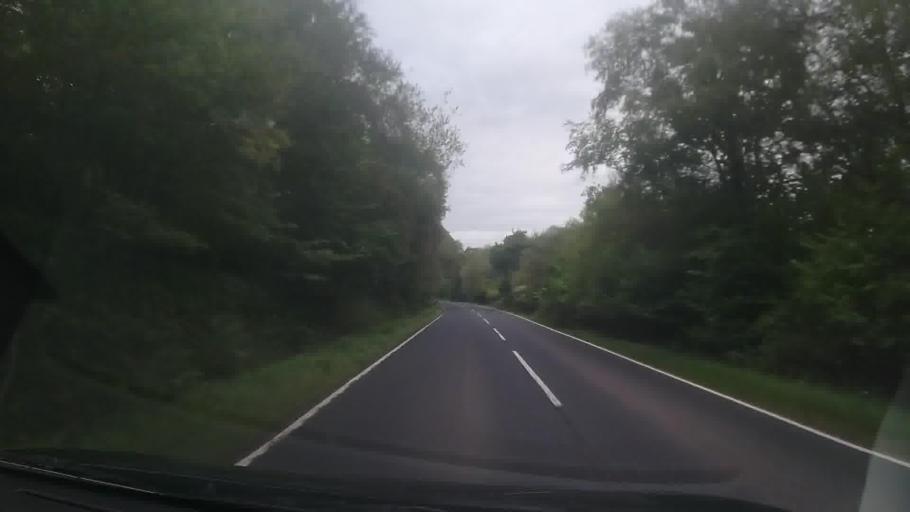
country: GB
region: Scotland
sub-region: Argyll and Bute
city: Garelochhead
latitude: 56.2102
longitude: -5.0555
